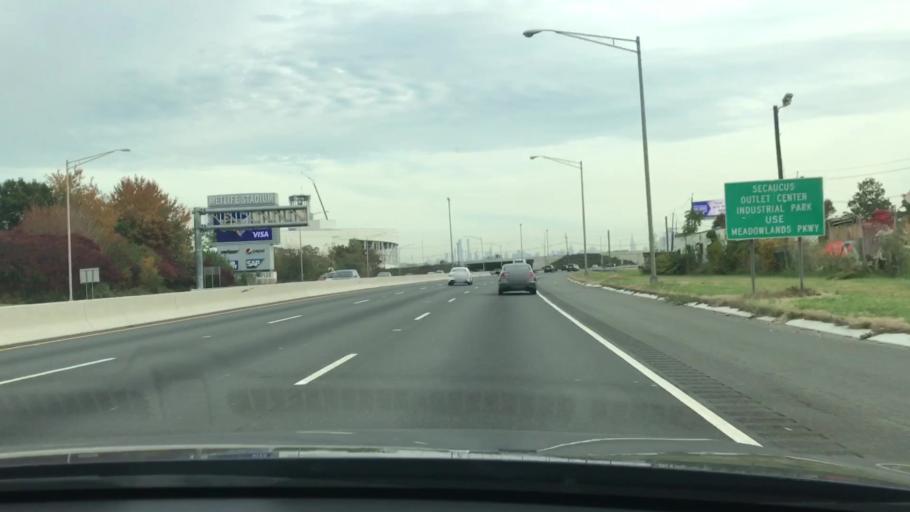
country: US
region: New Jersey
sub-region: Hudson County
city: Secaucus
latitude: 40.8078
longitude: -74.0782
